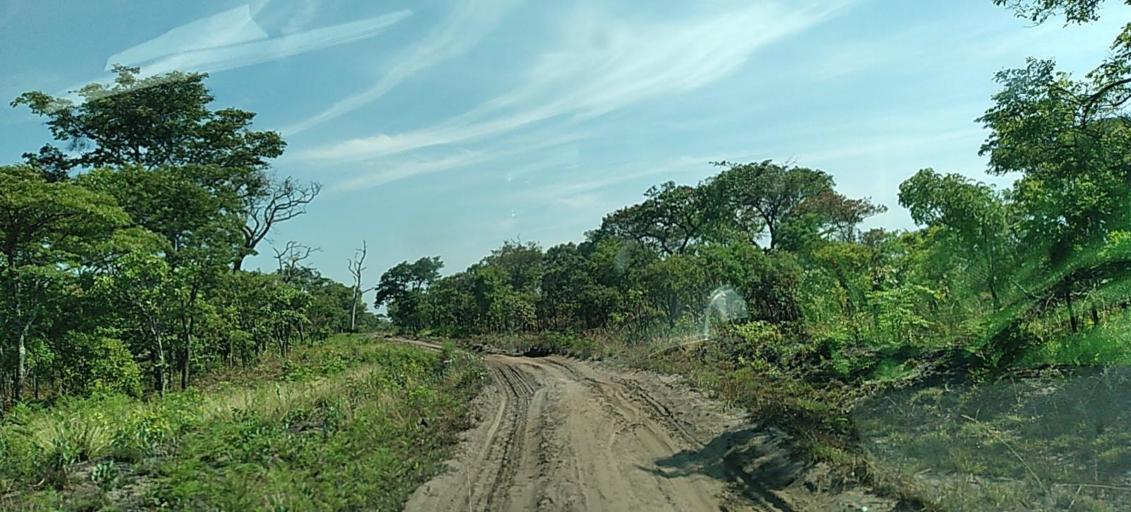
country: ZM
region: North-Western
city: Mwinilunga
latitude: -11.7948
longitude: 25.1675
